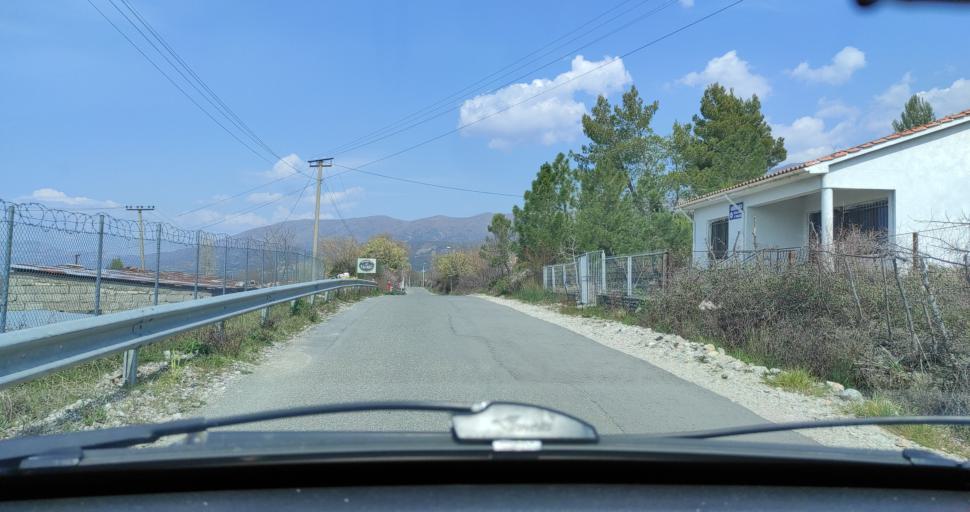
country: AL
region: Lezhe
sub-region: Rrethi i Lezhes
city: Kallmeti i Madh
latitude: 41.8534
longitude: 19.6944
